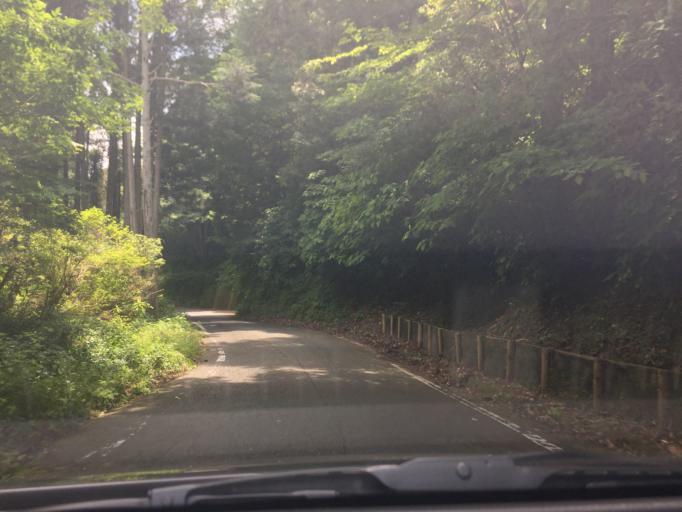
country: JP
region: Shizuoka
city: Shimoda
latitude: 34.7017
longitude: 138.7997
